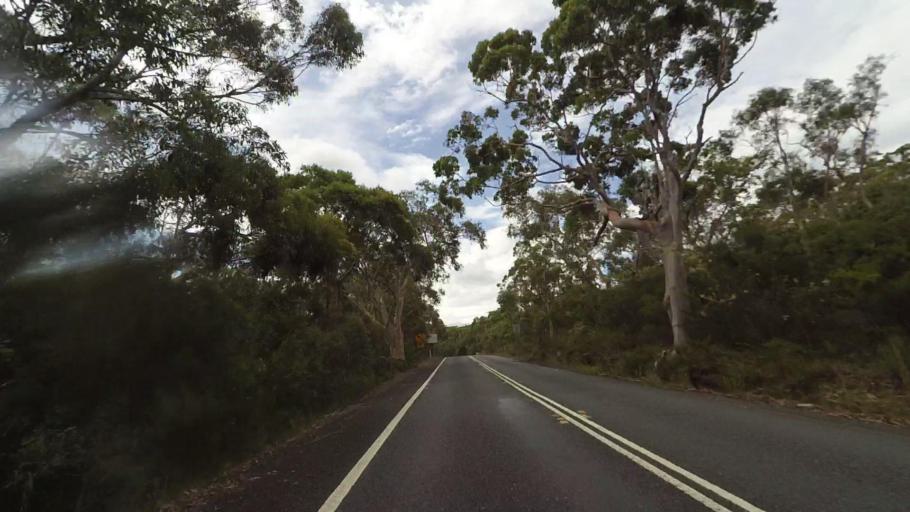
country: AU
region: New South Wales
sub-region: Sutherland Shire
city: Grays Point
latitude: -34.1162
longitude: 151.0693
